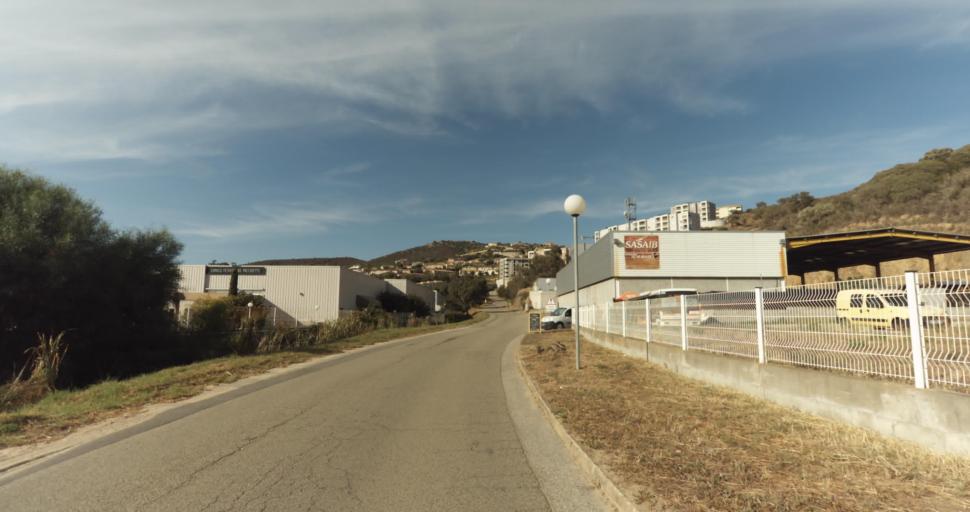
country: FR
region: Corsica
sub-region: Departement de la Corse-du-Sud
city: Afa
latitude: 41.9312
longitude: 8.7908
